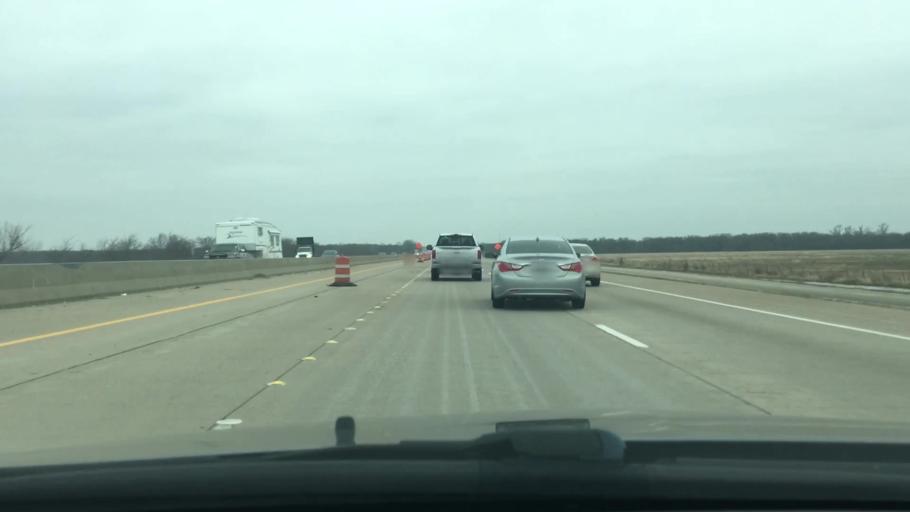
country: US
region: Texas
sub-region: Navarro County
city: Corsicana
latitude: 32.1732
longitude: -96.4706
